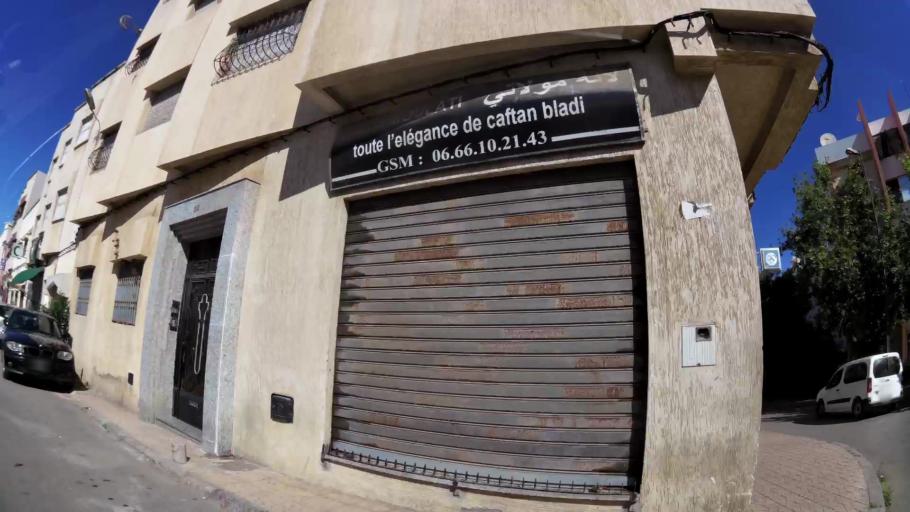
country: MA
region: Rabat-Sale-Zemmour-Zaer
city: Sale
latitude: 34.0674
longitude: -6.7941
